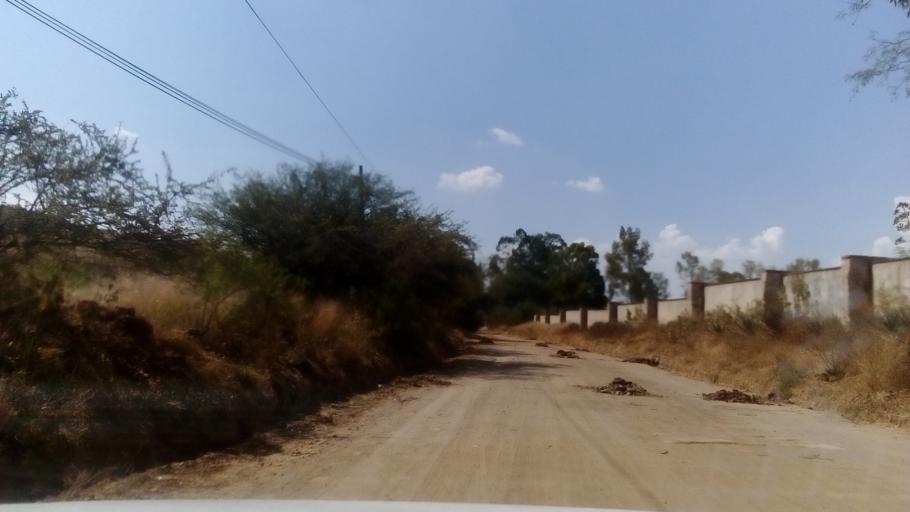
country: MX
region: Guanajuato
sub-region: Silao de la Victoria
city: San Francisco (Banos de Agua Caliente)
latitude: 21.0780
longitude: -101.4957
